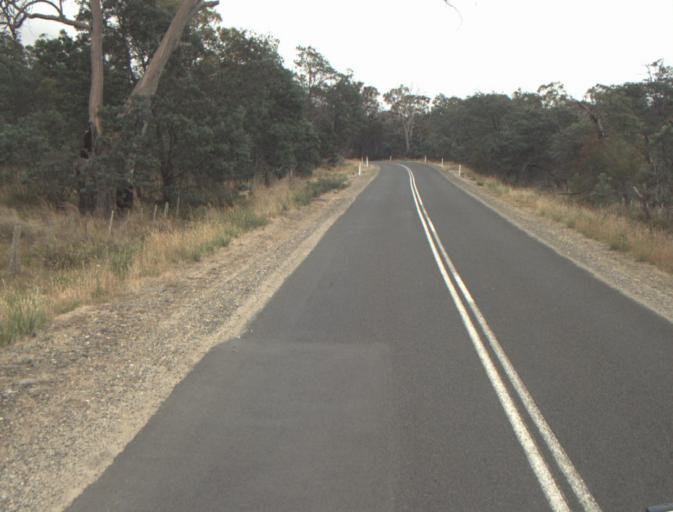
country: AU
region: Tasmania
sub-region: Northern Midlands
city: Evandale
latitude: -41.5114
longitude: 147.3423
